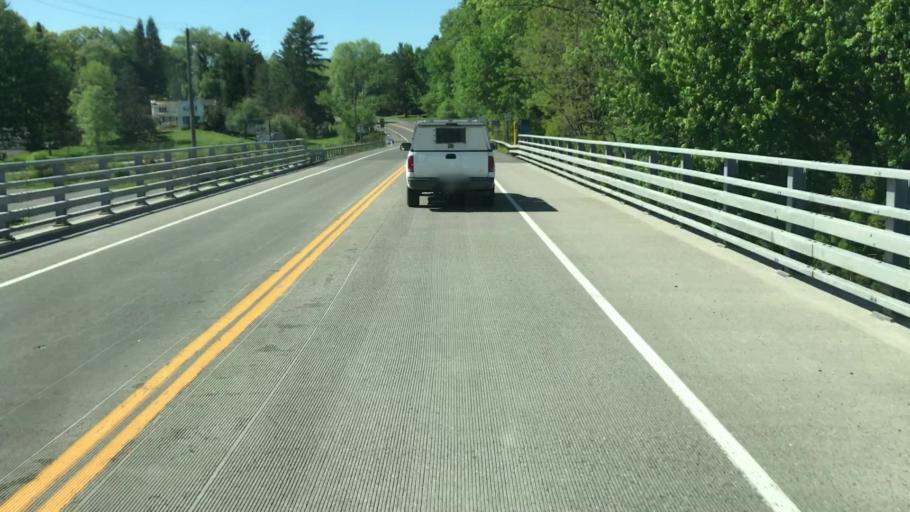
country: US
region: New York
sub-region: Onondaga County
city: Seneca Knolls
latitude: 43.1304
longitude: -76.2536
